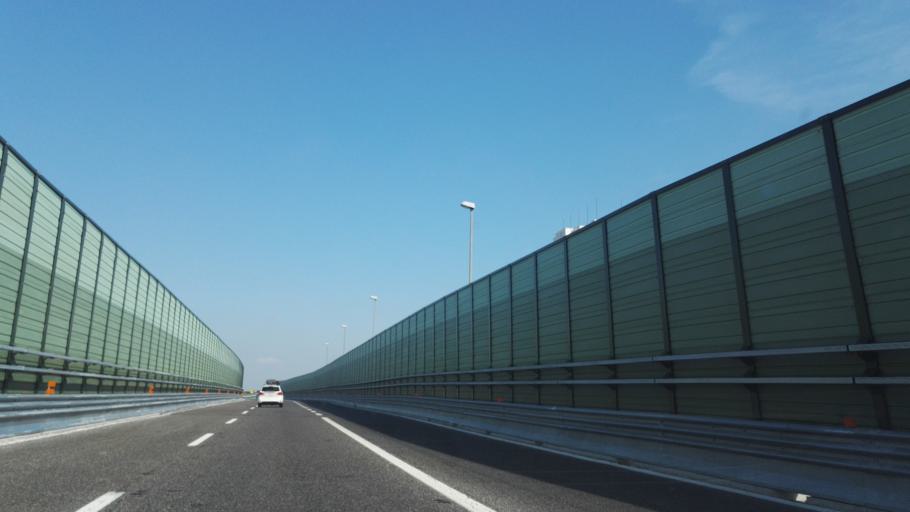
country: IT
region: Apulia
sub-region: Provincia di Bari
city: Modugno
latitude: 41.0911
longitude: 16.7820
